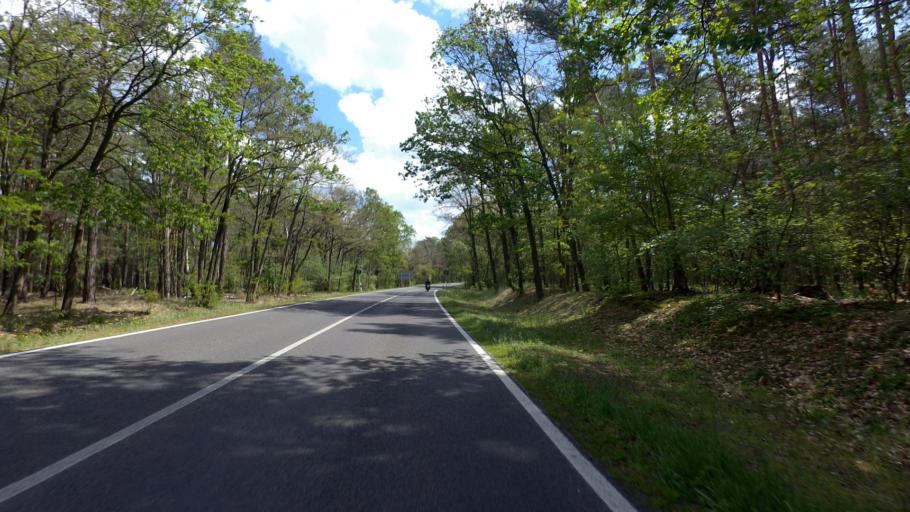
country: DE
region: Brandenburg
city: Neu Zauche
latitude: 51.9456
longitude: 14.0066
